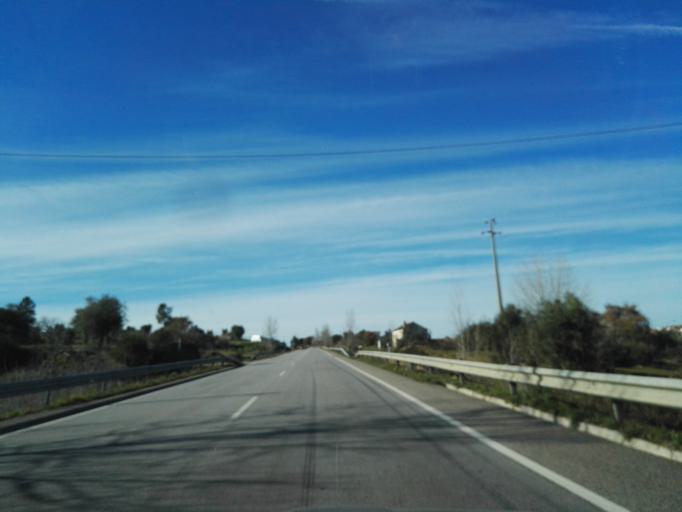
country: PT
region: Santarem
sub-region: Abrantes
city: Alferrarede
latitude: 39.4806
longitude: -8.0866
